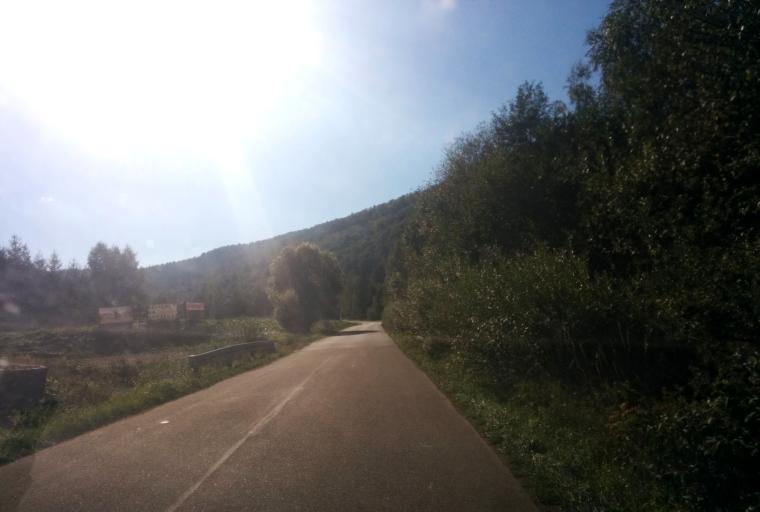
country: PL
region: Subcarpathian Voivodeship
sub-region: Powiat leski
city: Polanczyk
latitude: 49.2875
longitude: 22.4136
